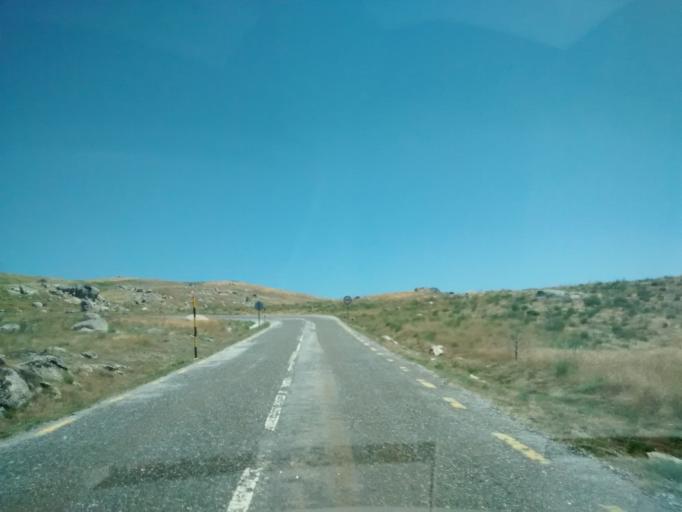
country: PT
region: Guarda
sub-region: Seia
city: Seia
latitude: 40.4136
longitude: -7.6408
